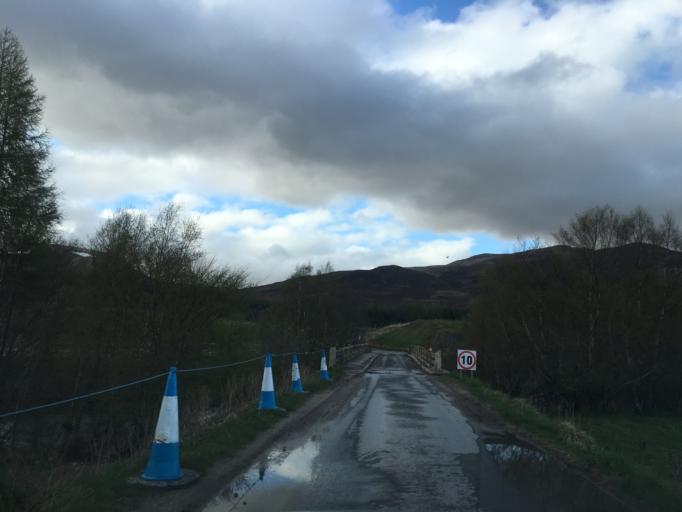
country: GB
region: Scotland
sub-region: Highland
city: Kingussie
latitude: 57.0118
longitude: -4.3326
